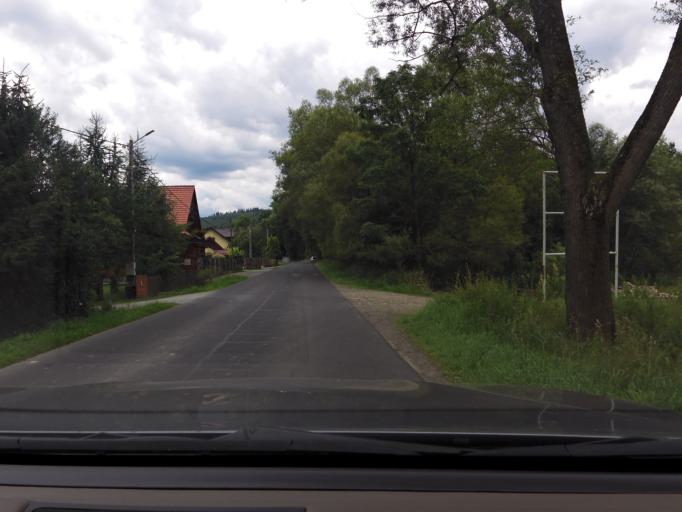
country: PL
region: Silesian Voivodeship
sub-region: Powiat zywiecki
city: Ujsoly
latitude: 49.4915
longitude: 19.1215
